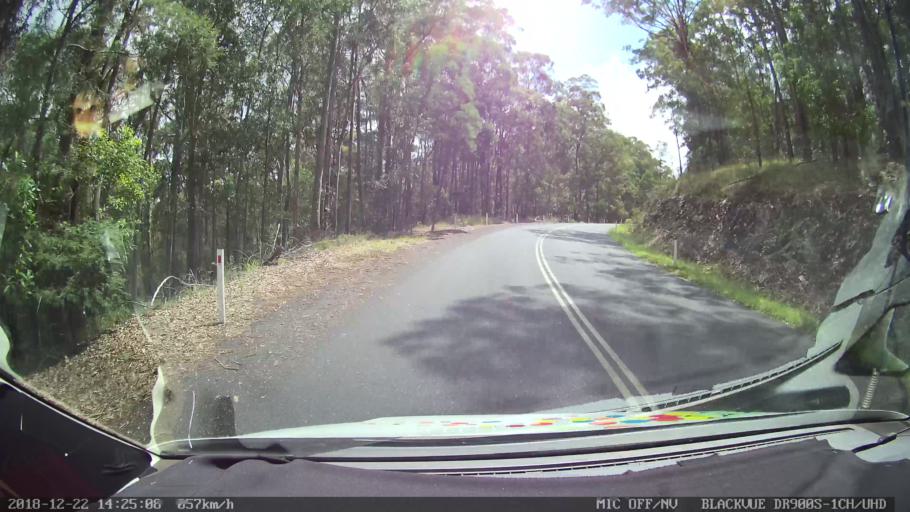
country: AU
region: New South Wales
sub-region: Bellingen
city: Dorrigo
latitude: -30.0496
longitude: 152.6413
